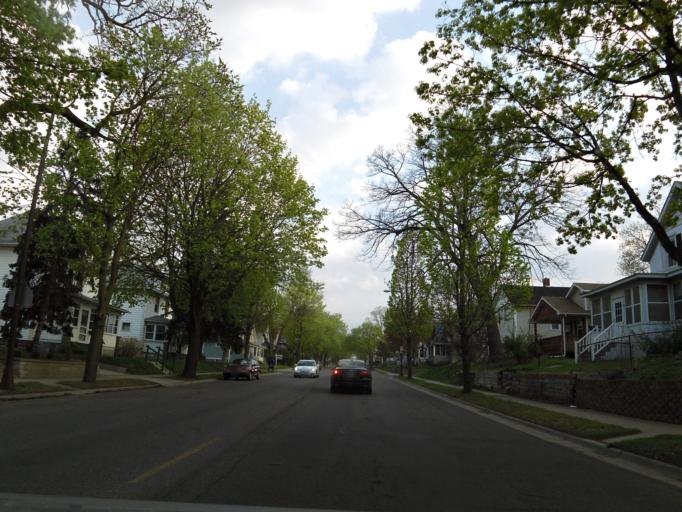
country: US
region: Minnesota
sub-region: Dakota County
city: West Saint Paul
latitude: 44.9242
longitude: -93.1019
